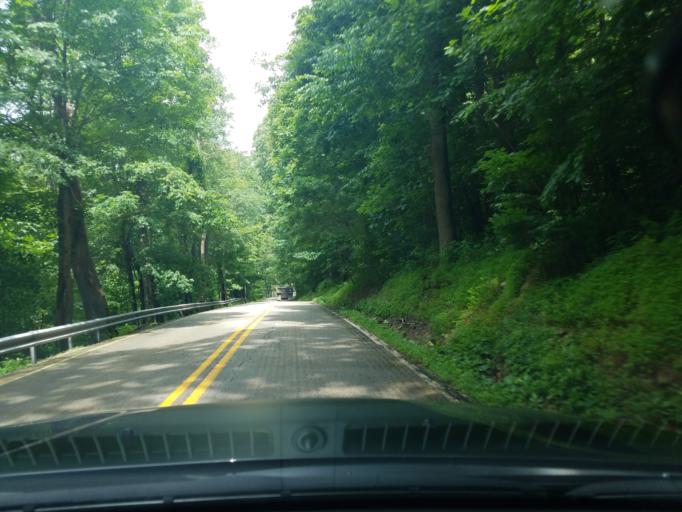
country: US
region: Pennsylvania
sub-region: Fayette County
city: Bear Rocks
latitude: 40.1675
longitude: -79.3614
